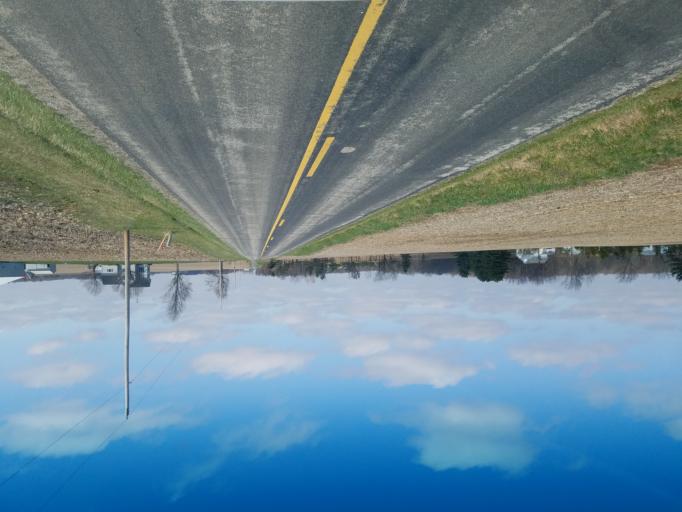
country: US
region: Ohio
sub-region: Crawford County
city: Bucyrus
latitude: 40.8866
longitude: -82.9018
